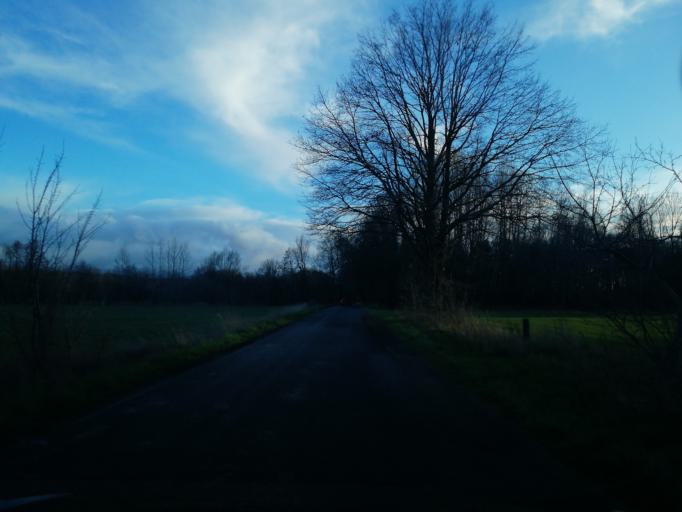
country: DE
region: Brandenburg
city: Calau
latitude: 51.7330
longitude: 13.9591
